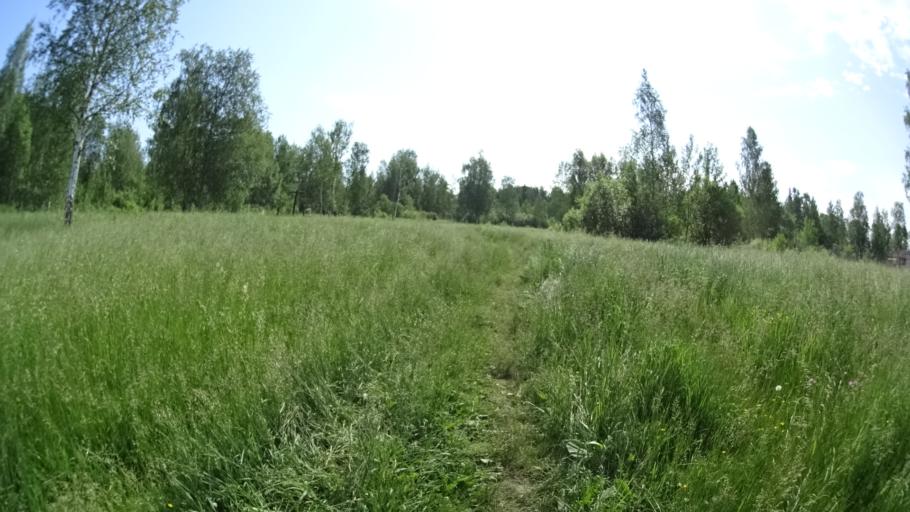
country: RU
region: Moskovskaya
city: Lesnoy
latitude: 56.0815
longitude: 37.9386
